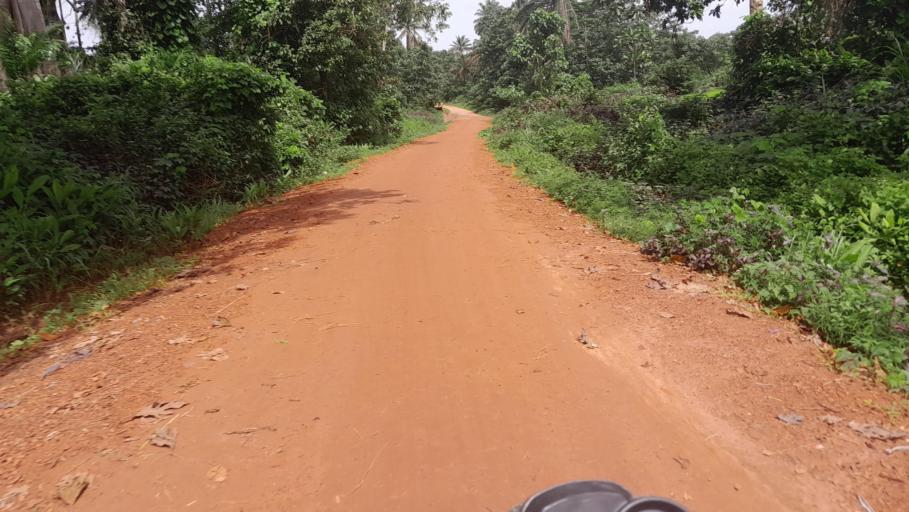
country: GN
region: Boke
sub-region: Boffa
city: Boffa
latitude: 10.0257
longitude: -13.8850
